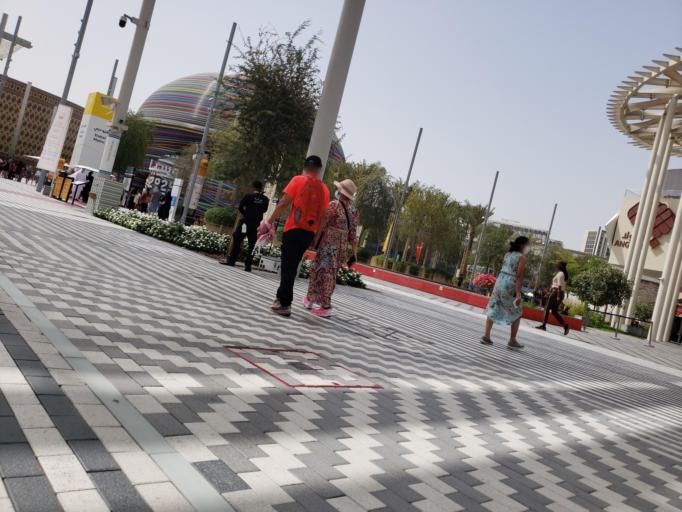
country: AE
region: Dubai
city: Dubai
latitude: 24.9600
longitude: 55.1485
